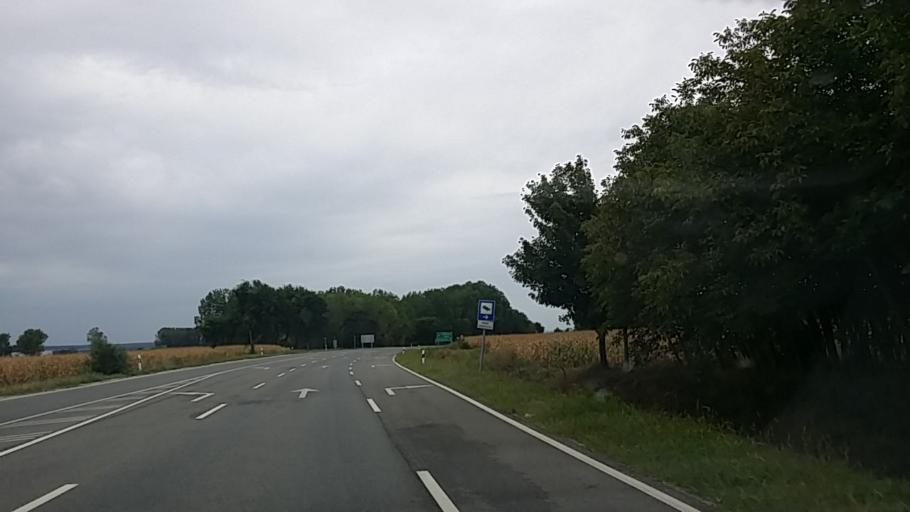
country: HU
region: Gyor-Moson-Sopron
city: Nagycenk
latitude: 47.5959
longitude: 16.7850
